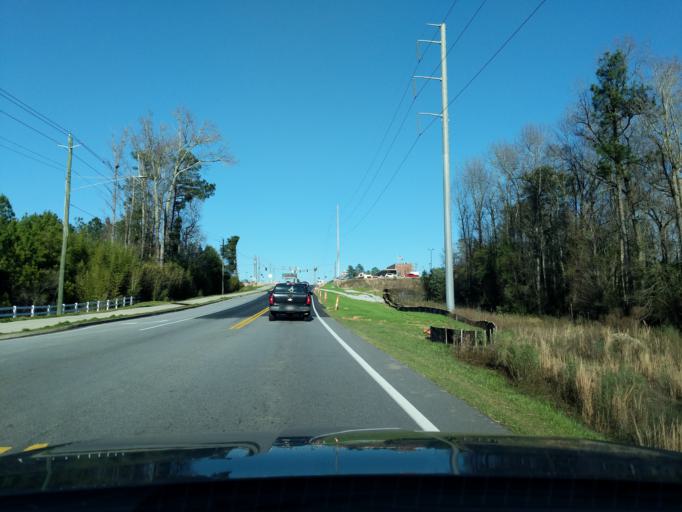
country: US
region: Georgia
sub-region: Columbia County
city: Grovetown
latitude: 33.4561
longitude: -82.2031
